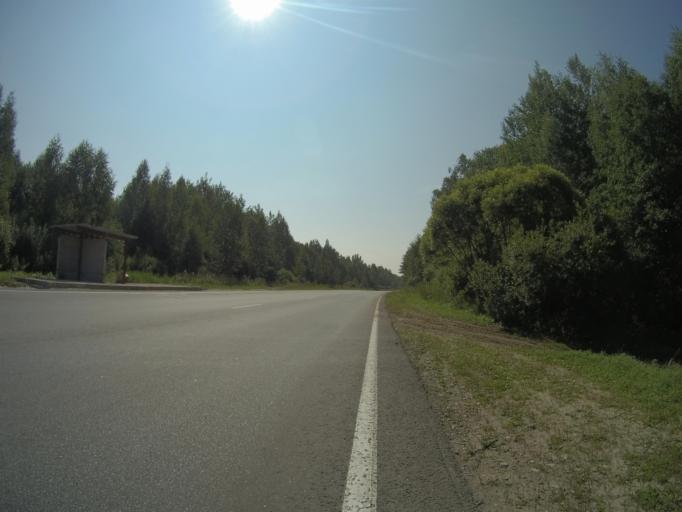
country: RU
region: Vladimir
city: Anopino
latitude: 55.8203
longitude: 40.6604
